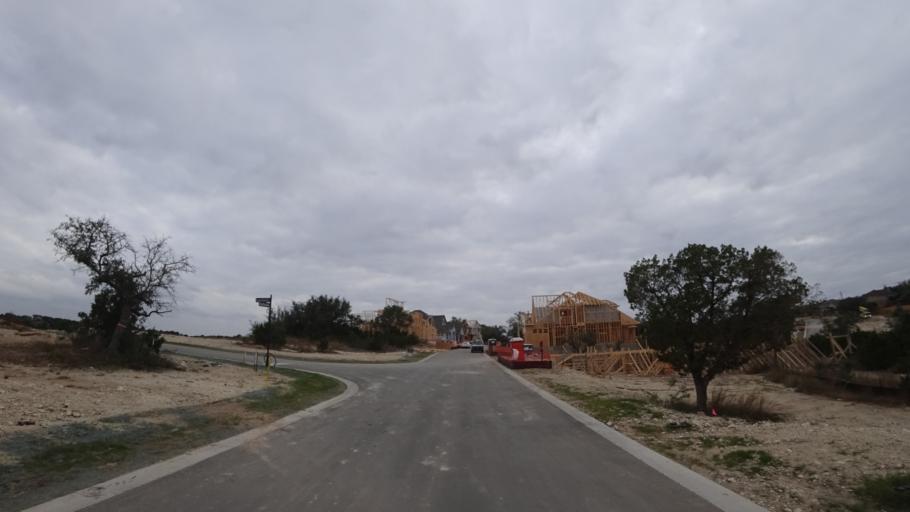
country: US
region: Texas
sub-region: Travis County
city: Bee Cave
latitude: 30.3161
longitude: -97.9133
